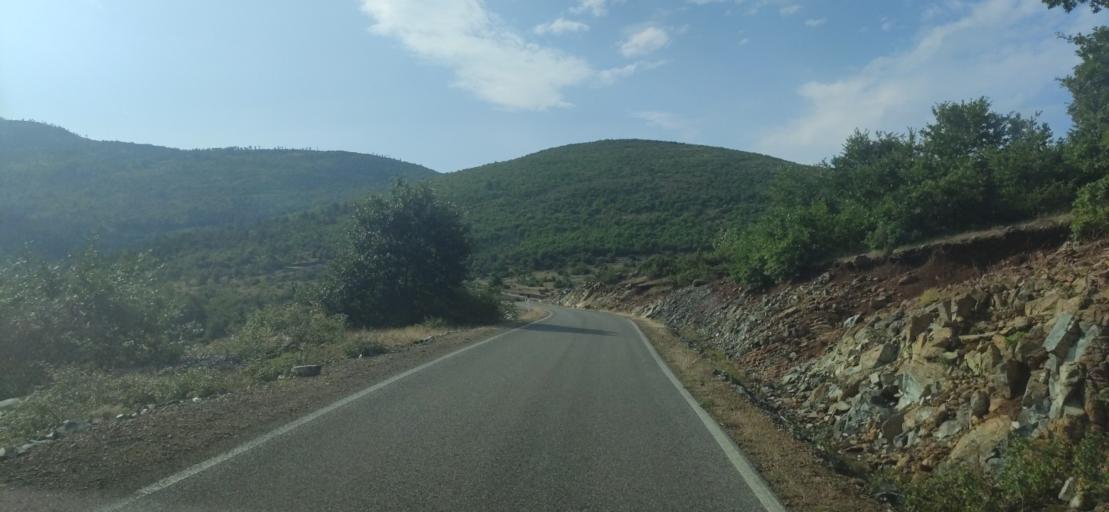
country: AL
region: Shkoder
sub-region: Rrethi i Pukes
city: Iballe
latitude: 42.1802
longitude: 20.0007
